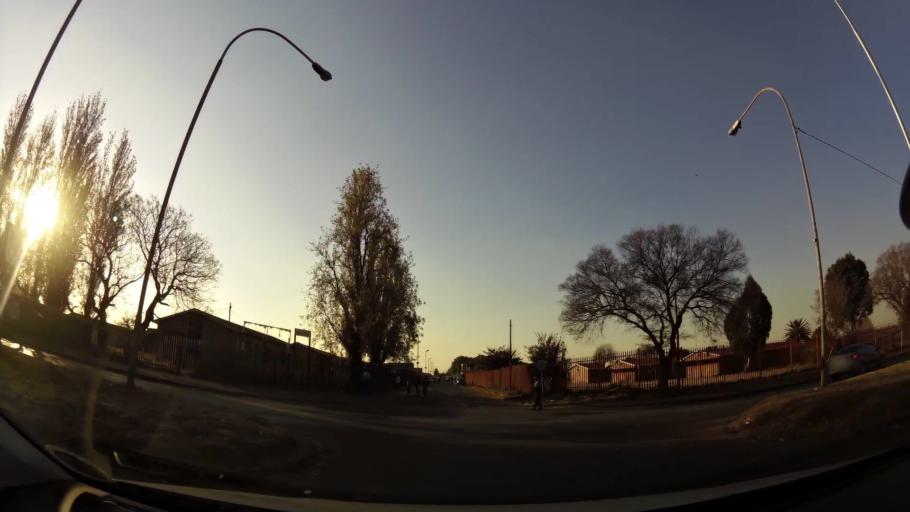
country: ZA
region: Gauteng
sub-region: City of Johannesburg Metropolitan Municipality
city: Soweto
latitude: -26.2521
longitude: 27.8785
